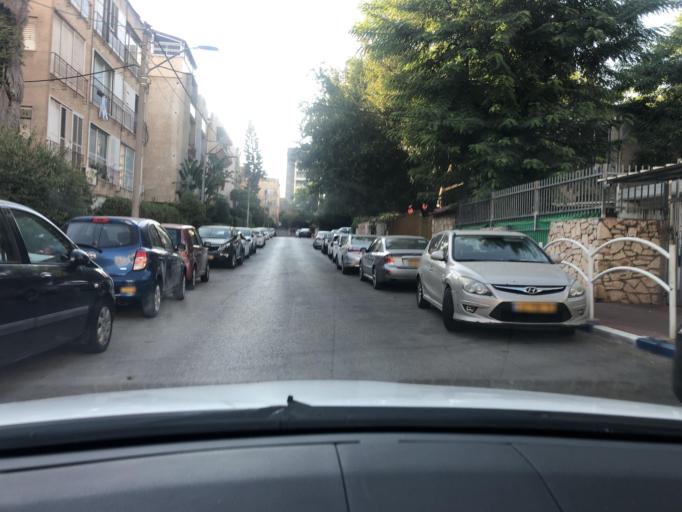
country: IL
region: Tel Aviv
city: Giv`atayim
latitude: 32.0648
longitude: 34.8227
